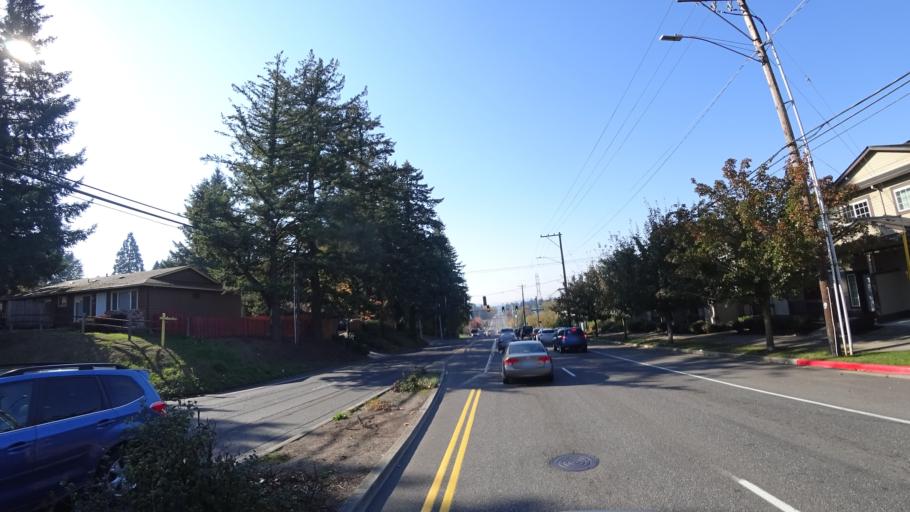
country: US
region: Oregon
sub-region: Multnomah County
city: Gresham
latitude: 45.5045
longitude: -122.4541
